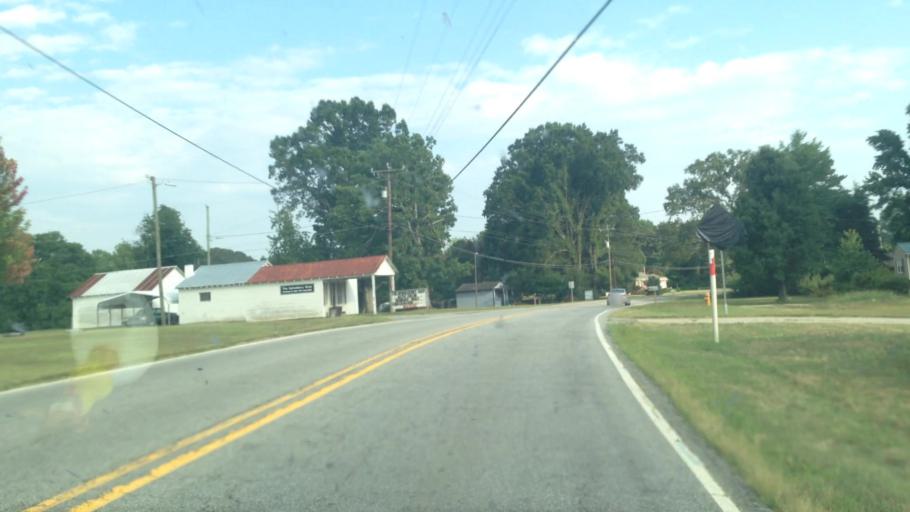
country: US
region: North Carolina
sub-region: Forsyth County
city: Kernersville
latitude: 36.0741
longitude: -80.0593
